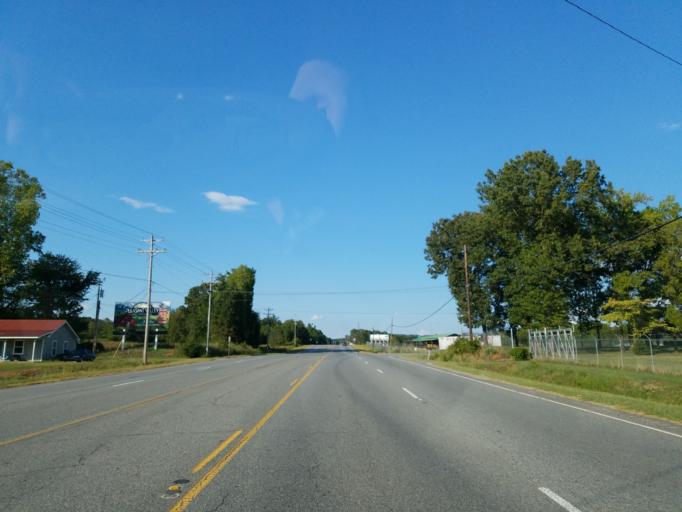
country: US
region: Georgia
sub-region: Murray County
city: Chatsworth
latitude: 34.8407
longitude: -84.7579
